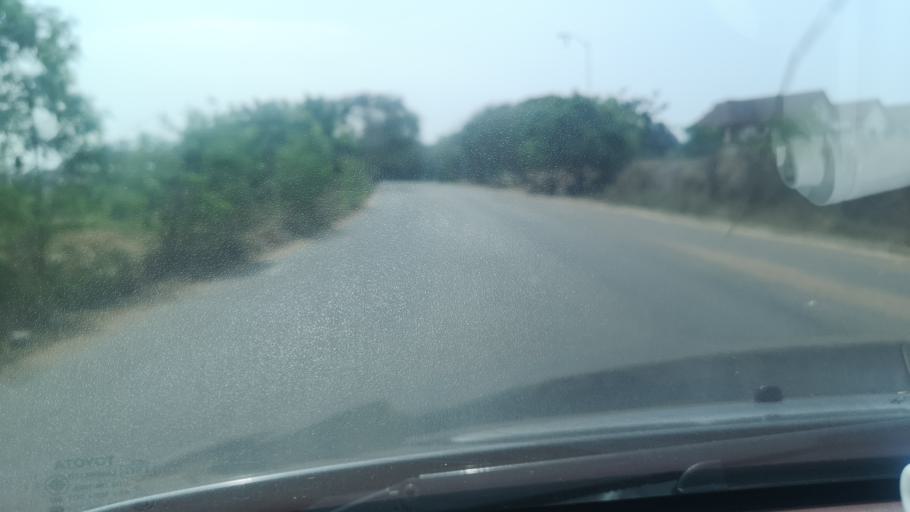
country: GH
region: Greater Accra
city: Nungua
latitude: 5.6144
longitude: -0.0579
